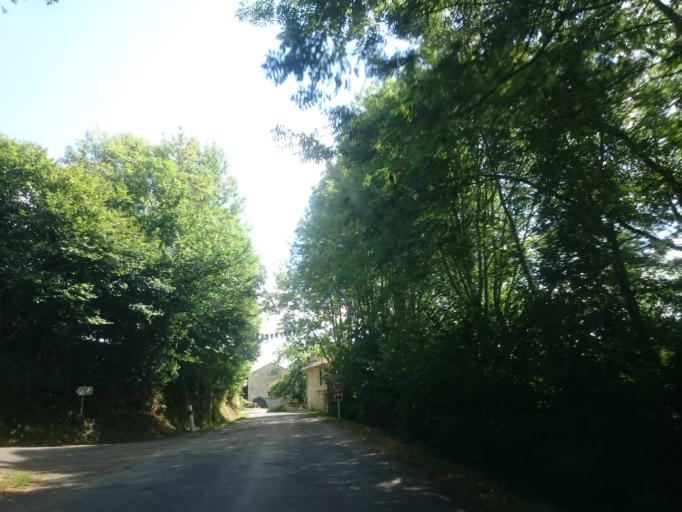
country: FR
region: Auvergne
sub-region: Departement du Cantal
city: Laroquebrou
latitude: 44.8943
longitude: 2.2079
